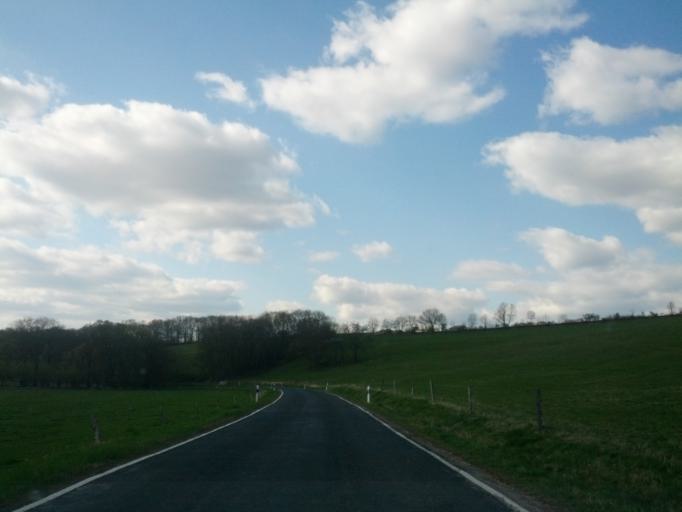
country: DE
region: Thuringia
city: Seebach
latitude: 50.9768
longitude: 10.4441
